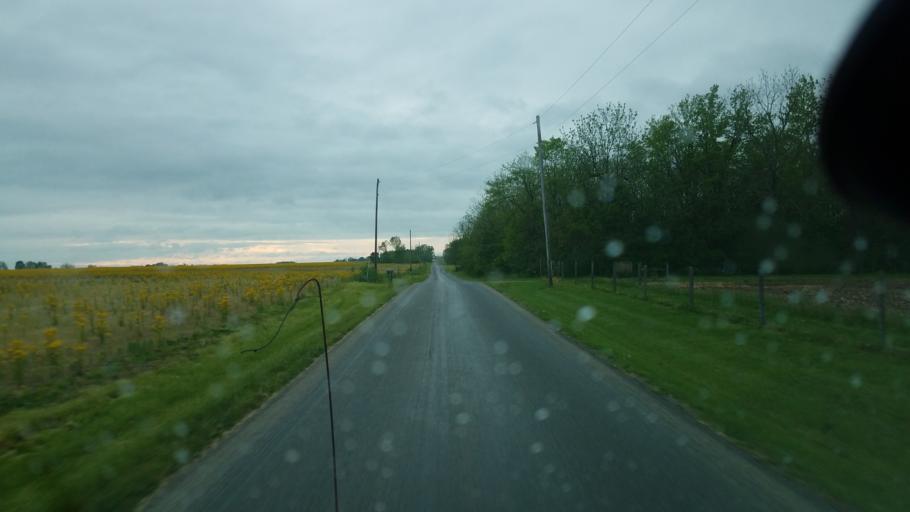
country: US
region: Ohio
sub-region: Highland County
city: Greenfield
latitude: 39.3223
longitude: -83.4227
